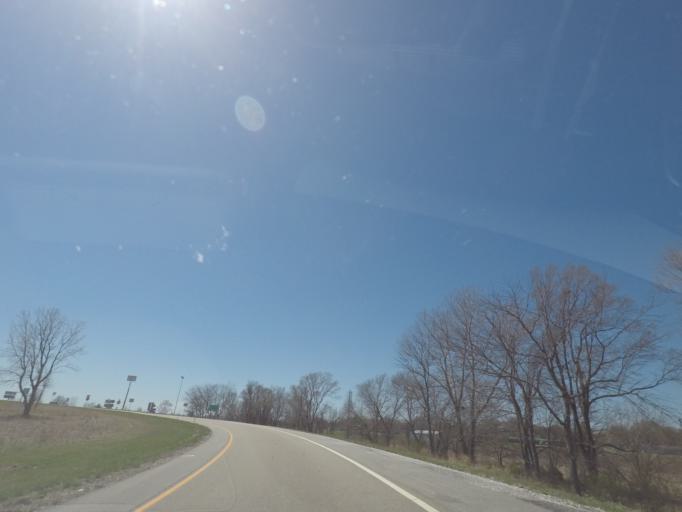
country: US
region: Illinois
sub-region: Logan County
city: Atlanta
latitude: 40.2610
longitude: -89.2219
